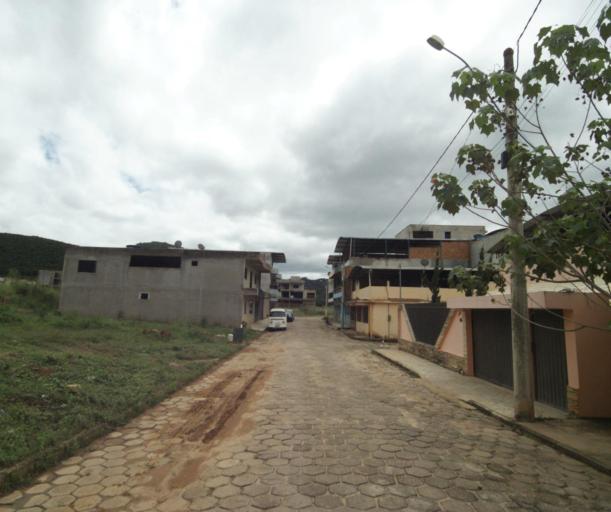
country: BR
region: Espirito Santo
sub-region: Irupi
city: Irupi
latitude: -20.3435
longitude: -41.6434
